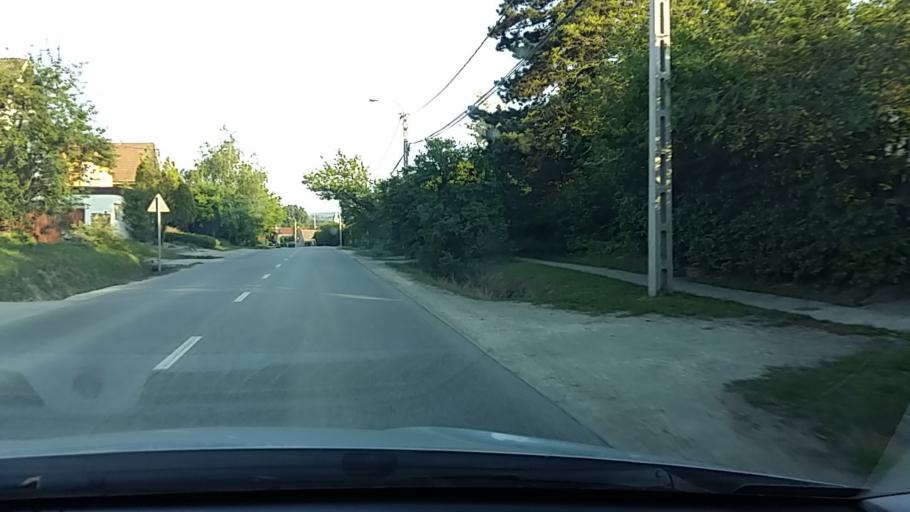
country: HU
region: Pest
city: Orbottyan
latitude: 47.6871
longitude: 19.2604
